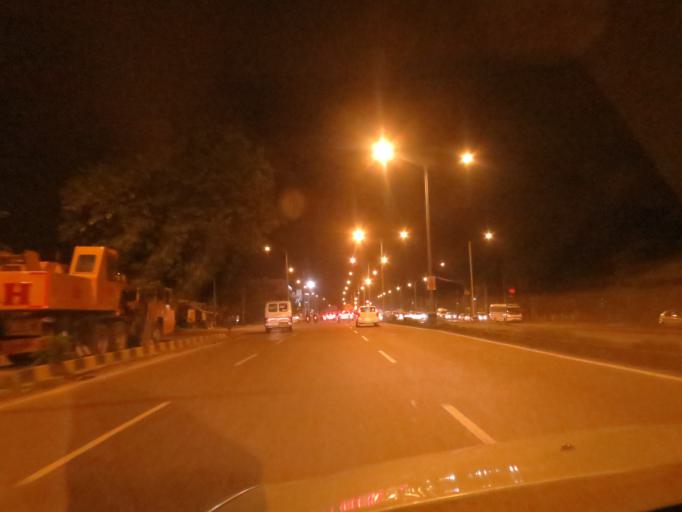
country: IN
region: Karnataka
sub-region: Bangalore Urban
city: Bangalore
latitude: 13.0105
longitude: 77.6624
